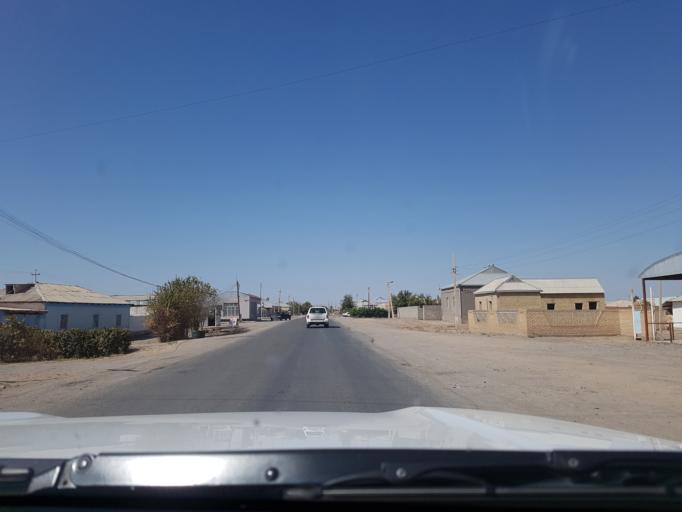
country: IR
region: Razavi Khorasan
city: Sarakhs
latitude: 36.5164
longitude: 61.2210
